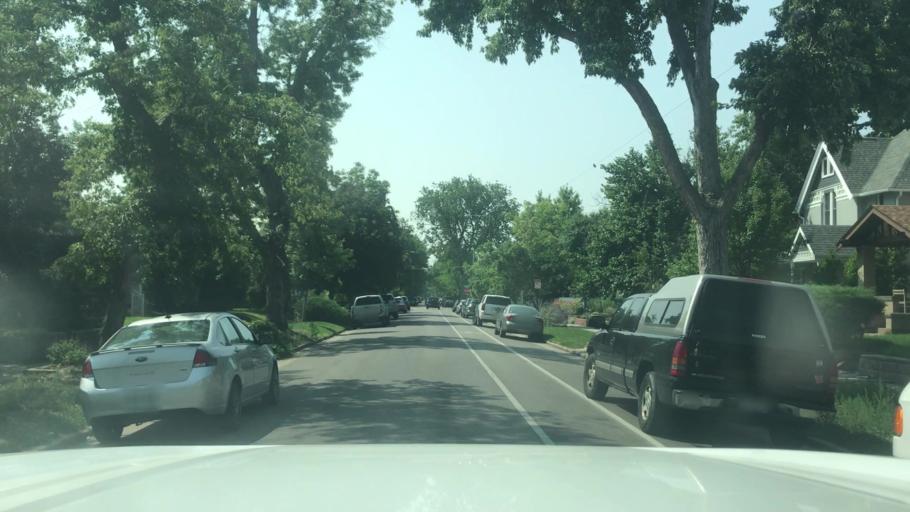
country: US
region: Colorado
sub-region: Denver County
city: Denver
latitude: 39.7016
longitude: -104.9793
